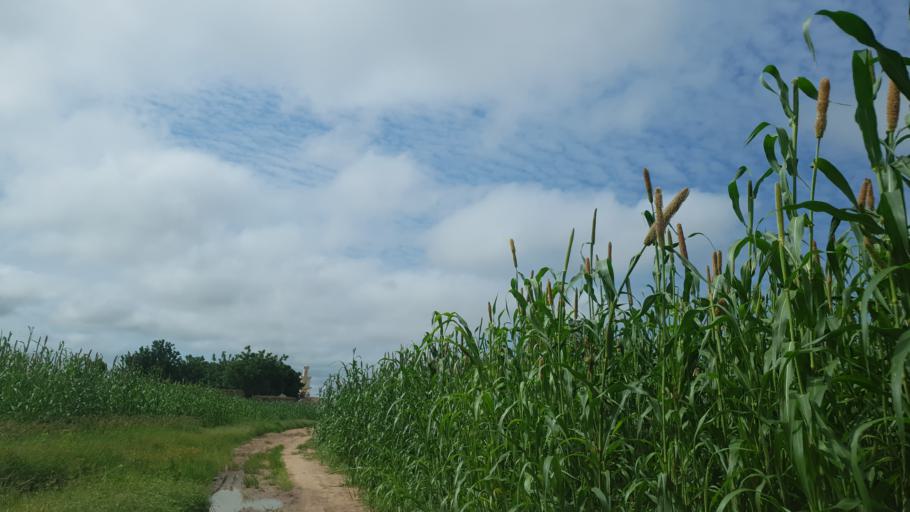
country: ML
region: Segou
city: Baroueli
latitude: 13.4863
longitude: -6.8961
